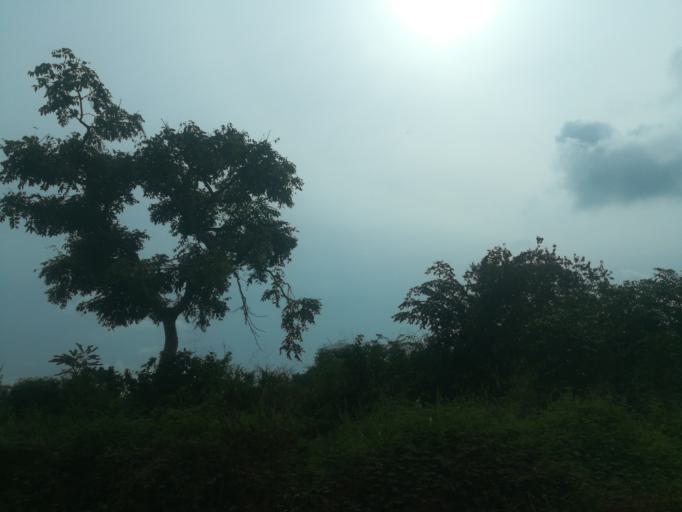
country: NG
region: Ogun
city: Ayetoro
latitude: 7.2878
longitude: 3.0840
